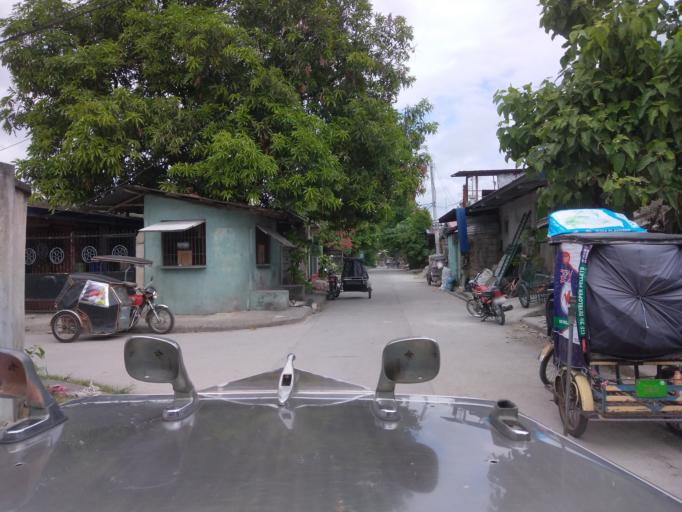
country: PH
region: Central Luzon
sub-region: Province of Pampanga
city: Pandacaqui
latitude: 15.1743
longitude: 120.6511
